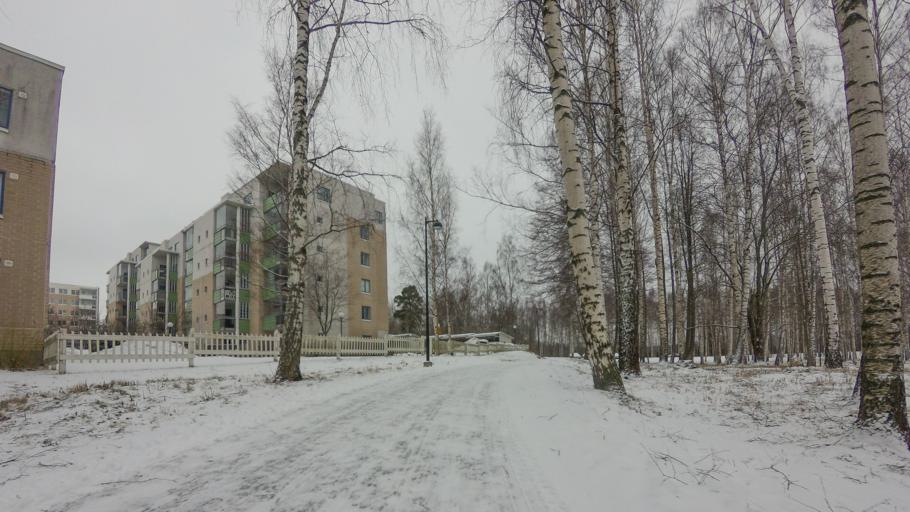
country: FI
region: Uusimaa
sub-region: Helsinki
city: Vantaa
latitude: 60.2010
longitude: 25.0689
